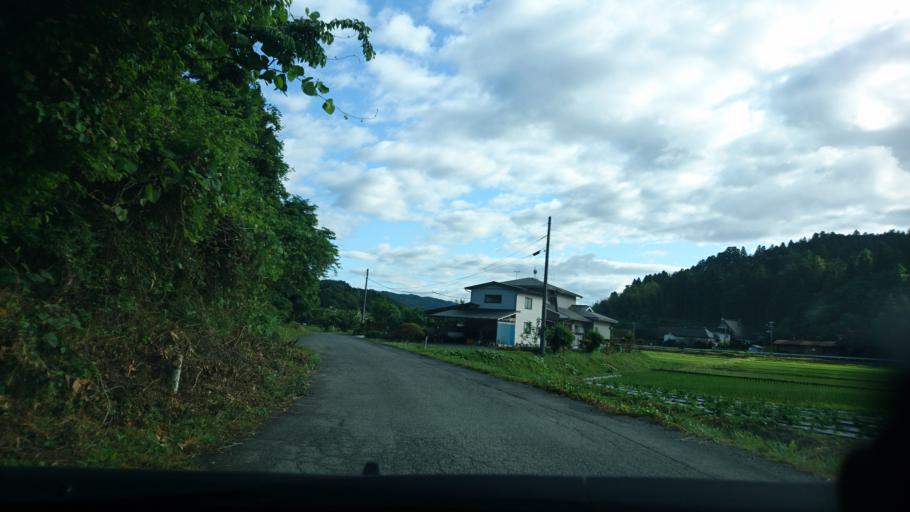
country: JP
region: Iwate
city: Ichinoseki
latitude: 38.8597
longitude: 141.2848
